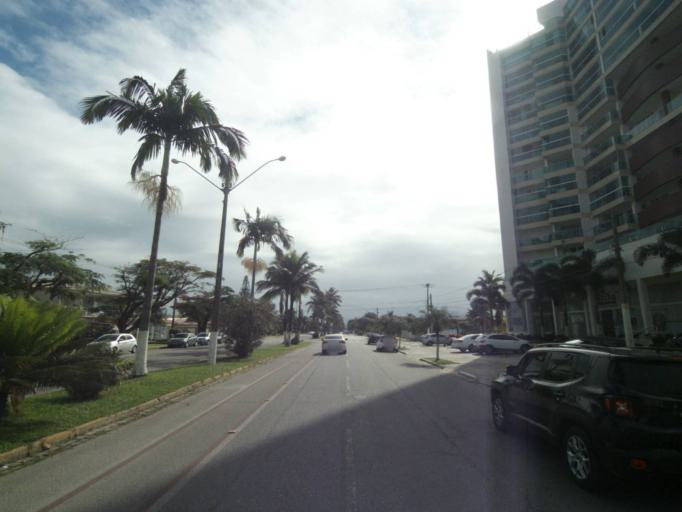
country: BR
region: Parana
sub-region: Paranagua
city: Paranagua
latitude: -25.5145
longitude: -48.5036
